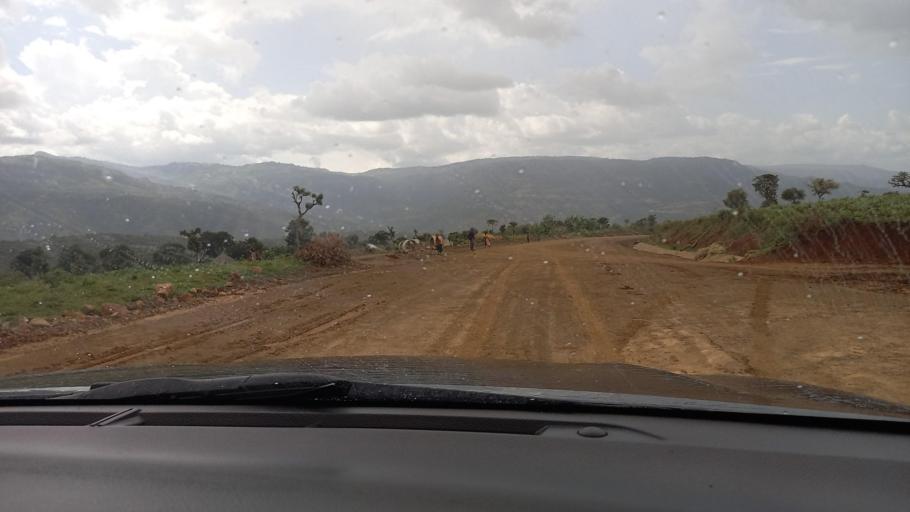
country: ET
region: Southern Nations, Nationalities, and People's Region
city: Mizan Teferi
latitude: 6.1762
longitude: 35.7048
